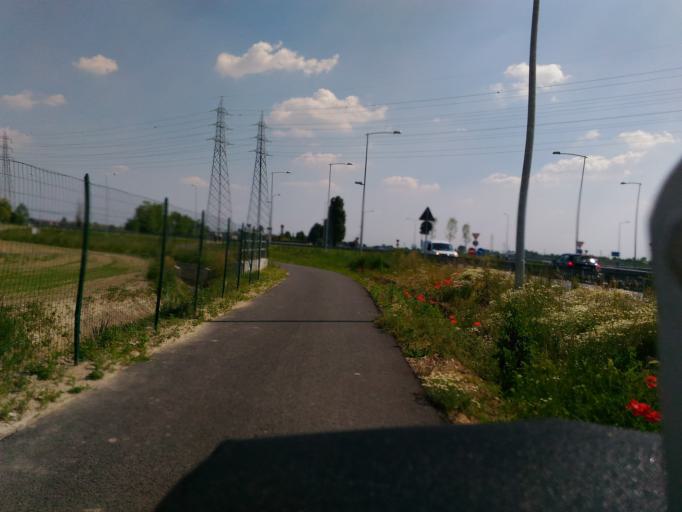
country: IT
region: Lombardy
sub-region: Citta metropolitana di Milano
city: Dresano
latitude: 45.3633
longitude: 9.3648
